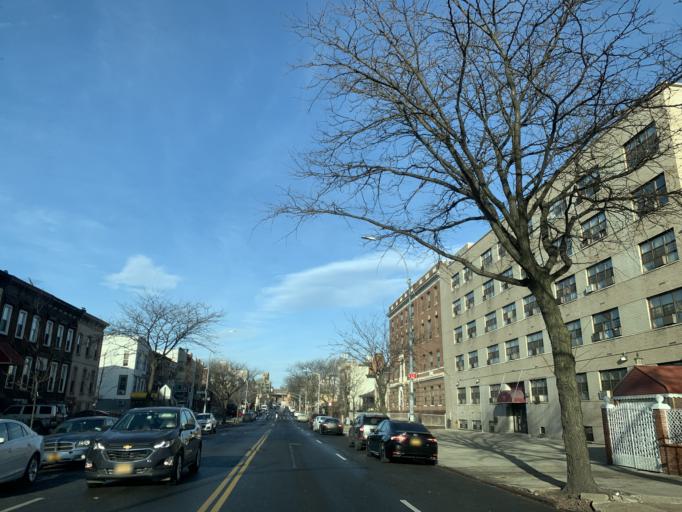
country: US
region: New York
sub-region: Kings County
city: Brooklyn
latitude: 40.6953
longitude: -73.9286
